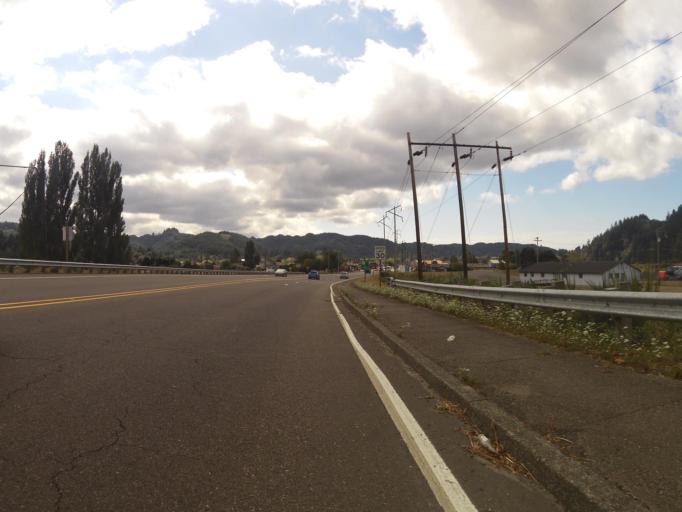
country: US
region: Oregon
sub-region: Douglas County
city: Reedsport
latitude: 43.7059
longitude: -124.1036
